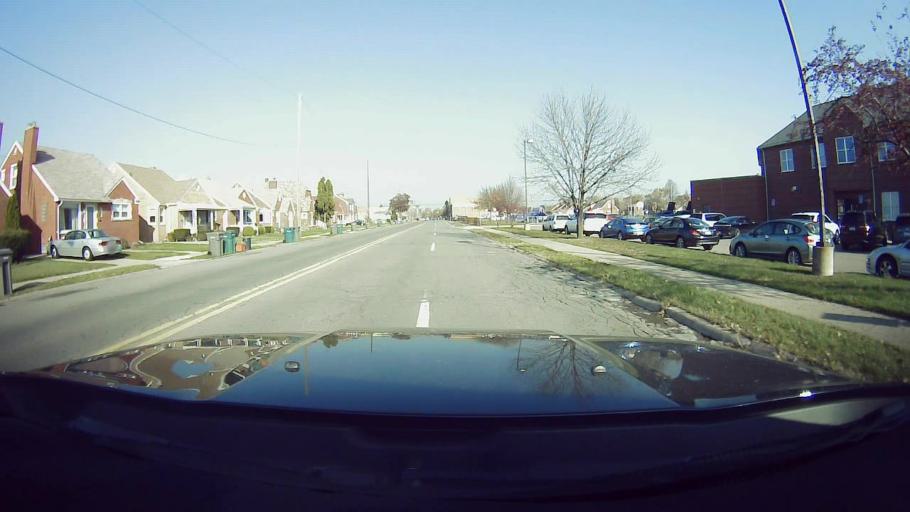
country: US
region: Michigan
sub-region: Wayne County
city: Dearborn
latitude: 42.3412
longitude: -83.1669
